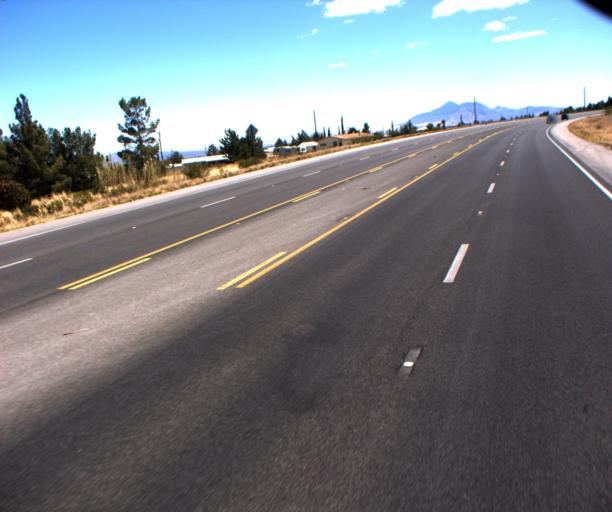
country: US
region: Arizona
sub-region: Cochise County
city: Sierra Vista Southeast
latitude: 31.4342
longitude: -110.2439
